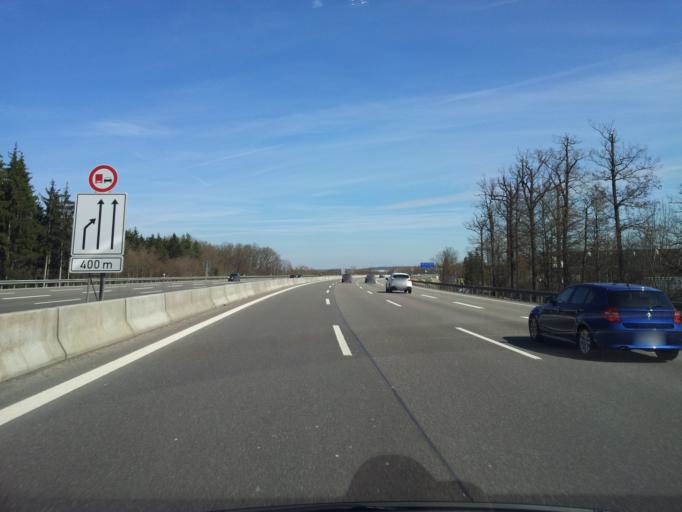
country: DE
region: Baden-Wuerttemberg
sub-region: Regierungsbezirk Stuttgart
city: Ehningen
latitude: 48.6767
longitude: 8.9644
